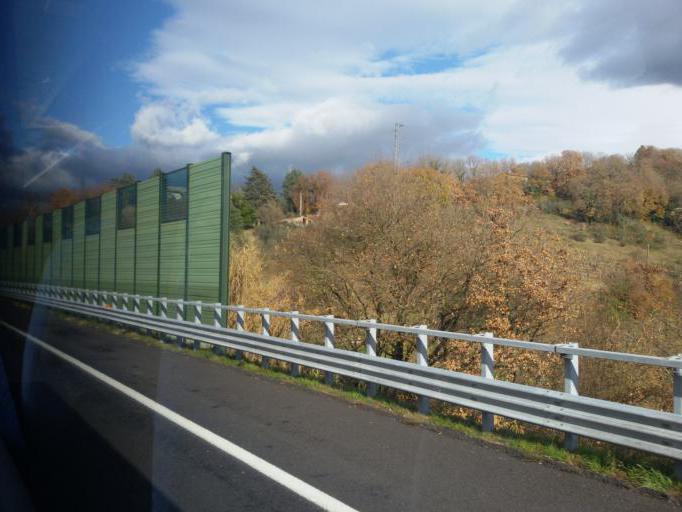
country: IT
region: Umbria
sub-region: Provincia di Terni
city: Baschi
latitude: 42.6837
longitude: 12.2115
